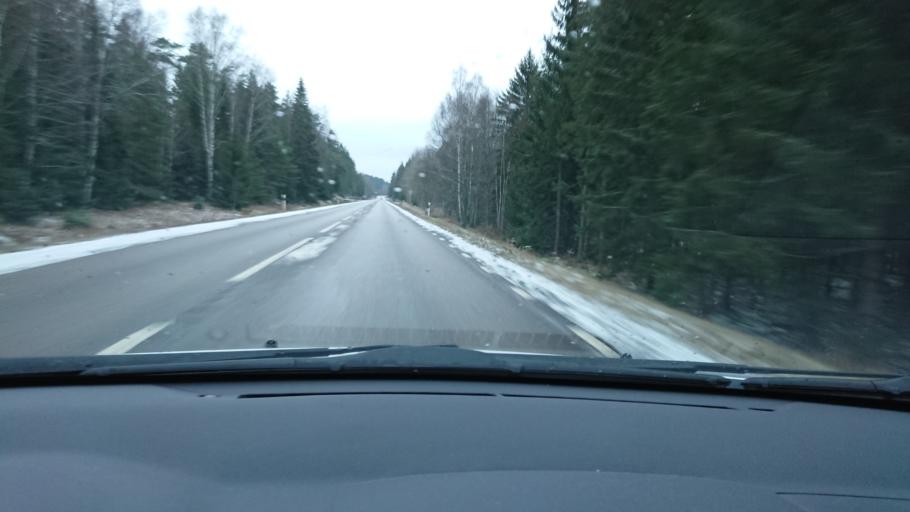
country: SE
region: Kalmar
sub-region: Hultsfreds Kommun
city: Hultsfred
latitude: 57.5434
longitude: 15.8462
